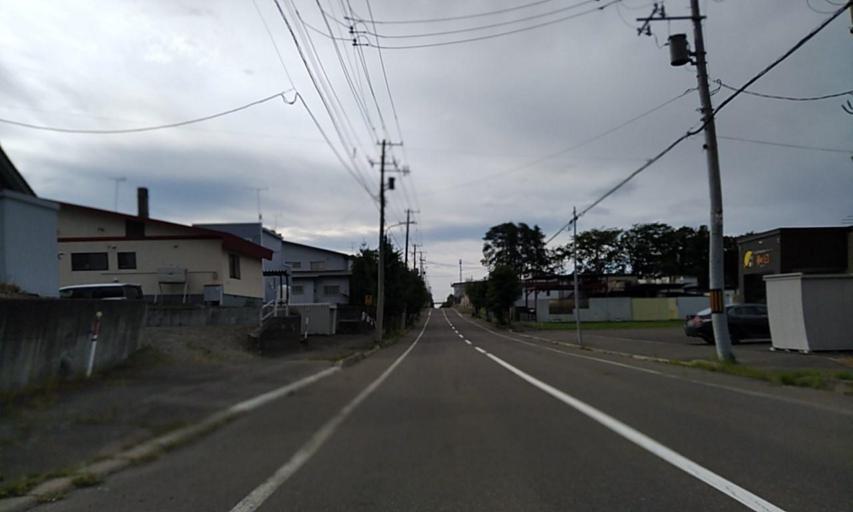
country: JP
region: Hokkaido
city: Obihiro
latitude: 42.9152
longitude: 143.0424
